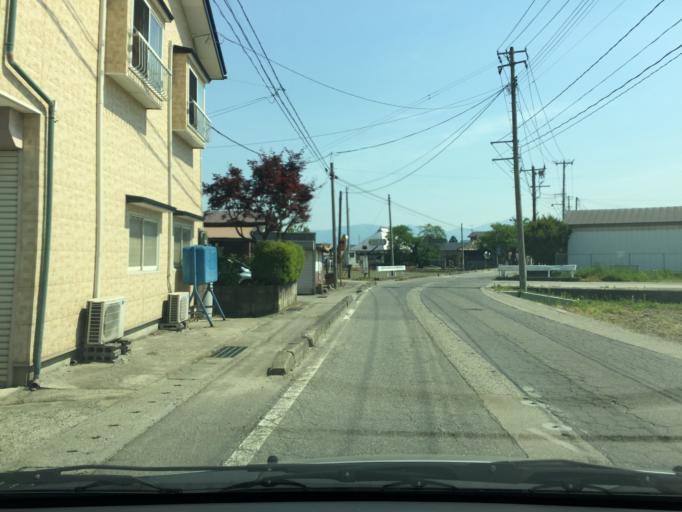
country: JP
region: Fukushima
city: Kitakata
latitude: 37.4628
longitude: 139.8955
